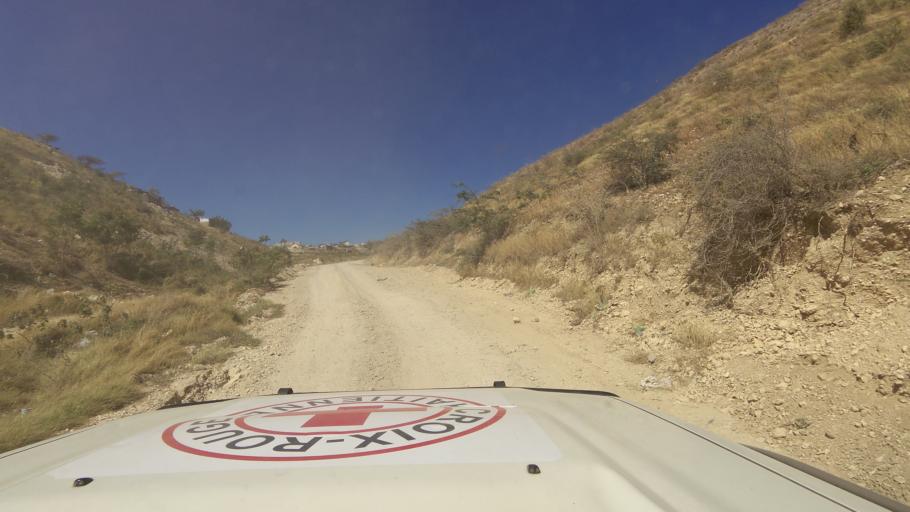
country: HT
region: Ouest
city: Croix des Bouquets
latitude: 18.6669
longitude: -72.2751
